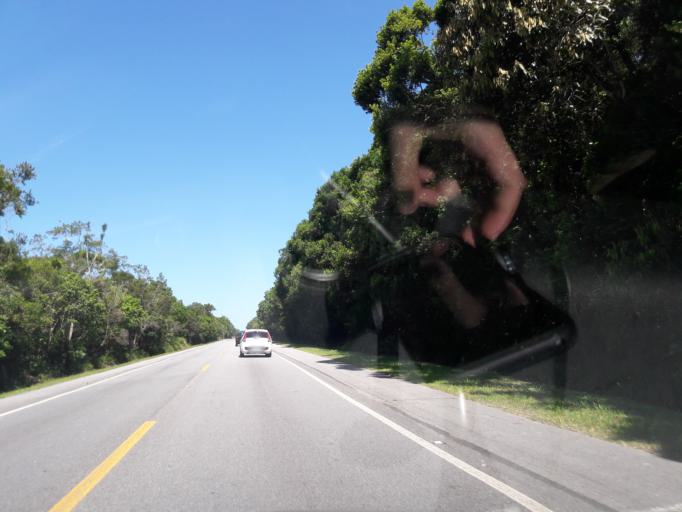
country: BR
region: Parana
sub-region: Pontal Do Parana
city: Pontal do Parana
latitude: -25.6244
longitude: -48.5432
